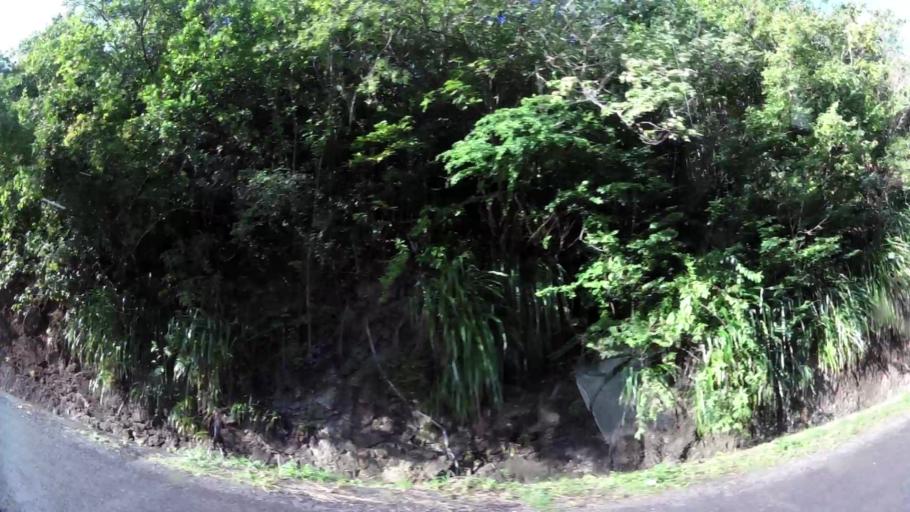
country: LC
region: Anse-la-Raye
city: Anse La Raye
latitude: 13.9265
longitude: -61.0439
